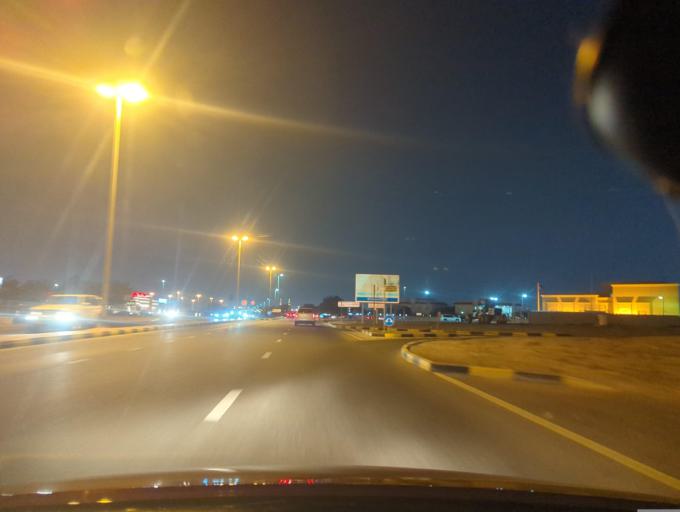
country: AE
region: Ash Shariqah
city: Sharjah
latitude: 25.3476
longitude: 55.4644
